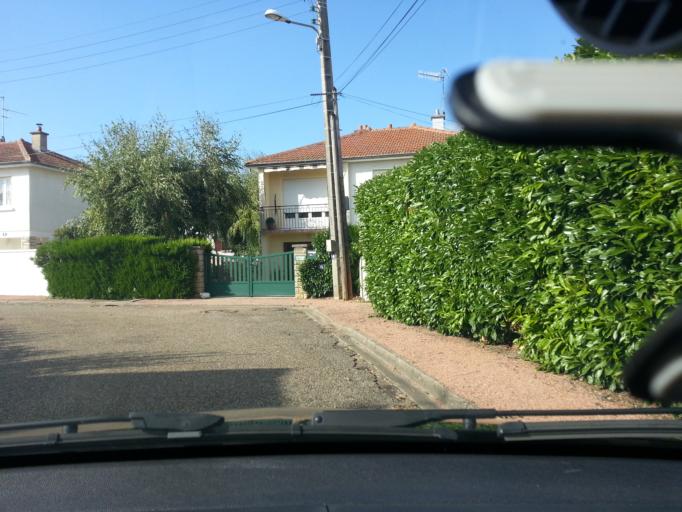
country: FR
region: Bourgogne
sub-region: Departement de Saone-et-Loire
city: Chatenoy-le-Royal
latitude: 46.7910
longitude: 4.8157
